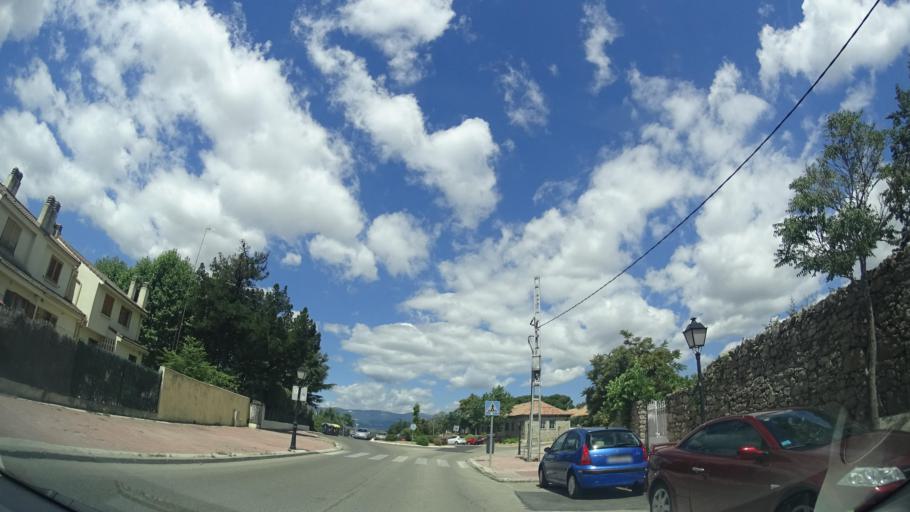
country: ES
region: Madrid
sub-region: Provincia de Madrid
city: Collado-Villalba
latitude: 40.6278
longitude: -3.9968
